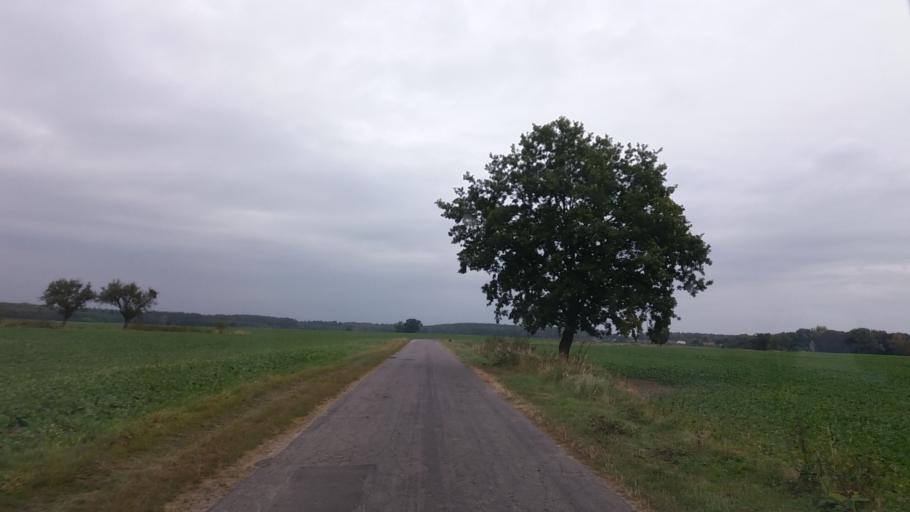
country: PL
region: West Pomeranian Voivodeship
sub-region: Powiat choszczenski
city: Krzecin
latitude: 52.9931
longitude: 15.5322
